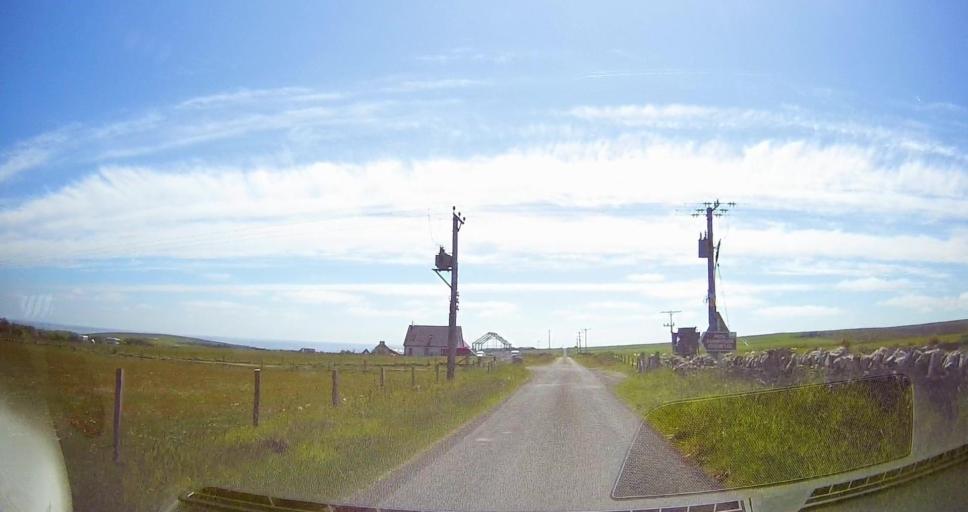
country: GB
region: Scotland
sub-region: Orkney Islands
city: Kirkwall
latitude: 58.8280
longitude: -2.9123
